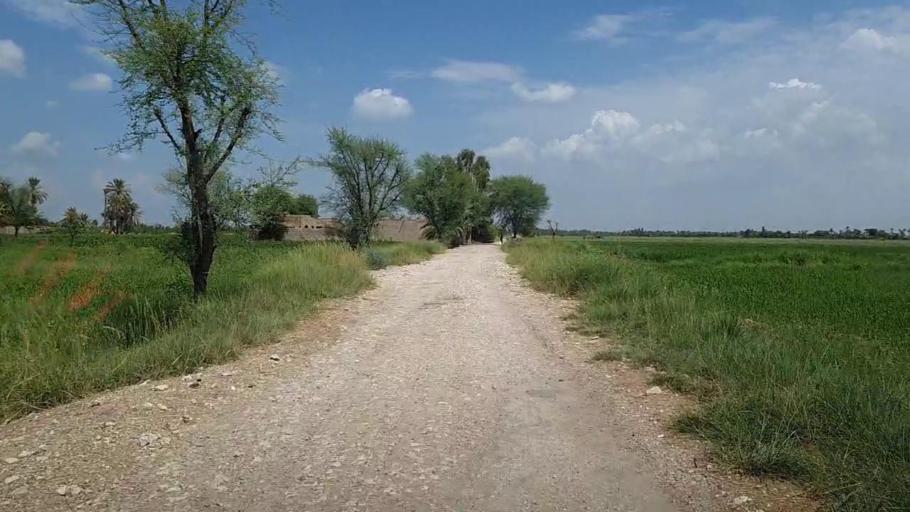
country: PK
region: Sindh
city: Bhiria
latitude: 26.9517
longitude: 68.2386
